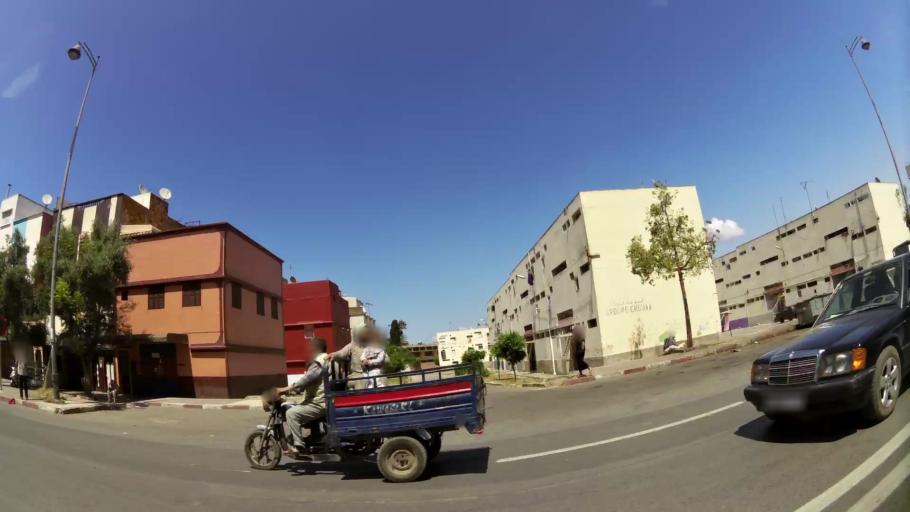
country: MA
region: Gharb-Chrarda-Beni Hssen
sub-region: Kenitra Province
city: Kenitra
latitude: 34.2472
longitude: -6.5536
